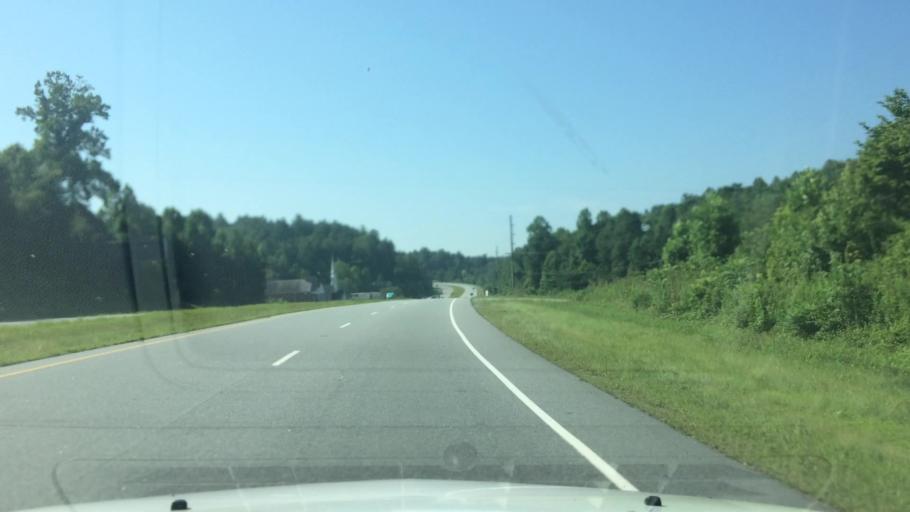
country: US
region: North Carolina
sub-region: Caldwell County
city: Lenoir
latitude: 35.9478
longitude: -81.5474
